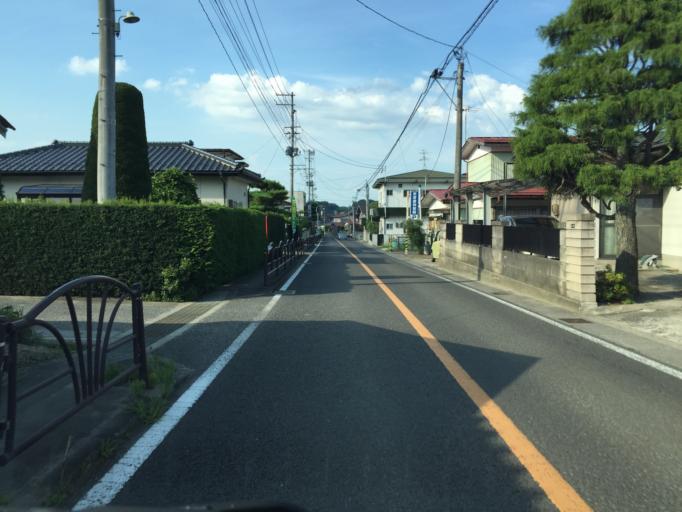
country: JP
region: Fukushima
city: Nihommatsu
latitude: 37.5565
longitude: 140.4121
